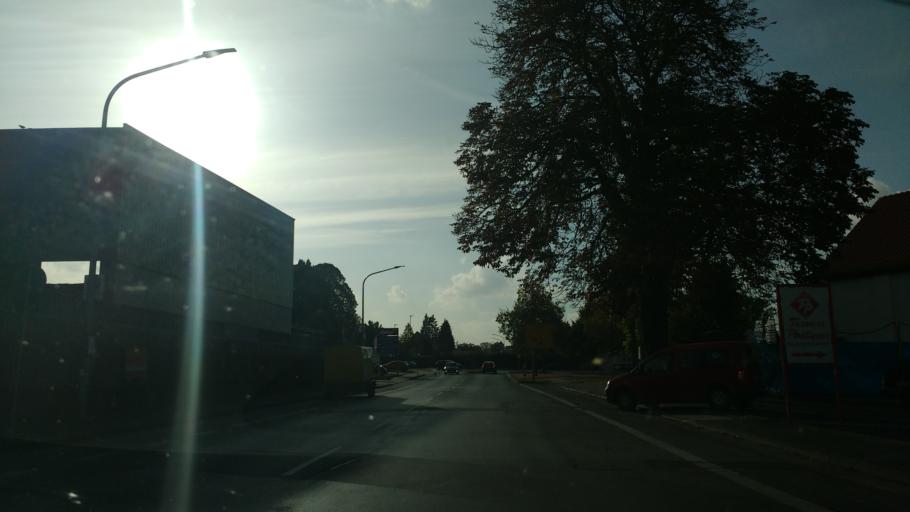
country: DE
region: North Rhine-Westphalia
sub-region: Regierungsbezirk Detmold
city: Lemgo
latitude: 52.0227
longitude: 8.8893
